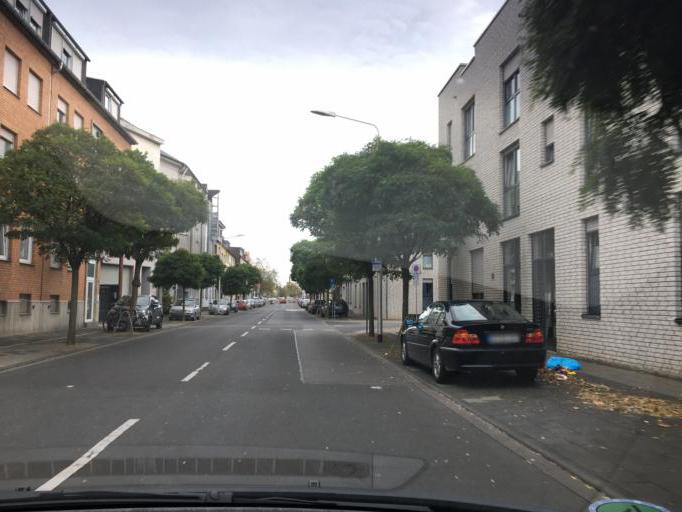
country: DE
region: North Rhine-Westphalia
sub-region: Regierungsbezirk Koln
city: Dueren
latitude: 50.7986
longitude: 6.4745
